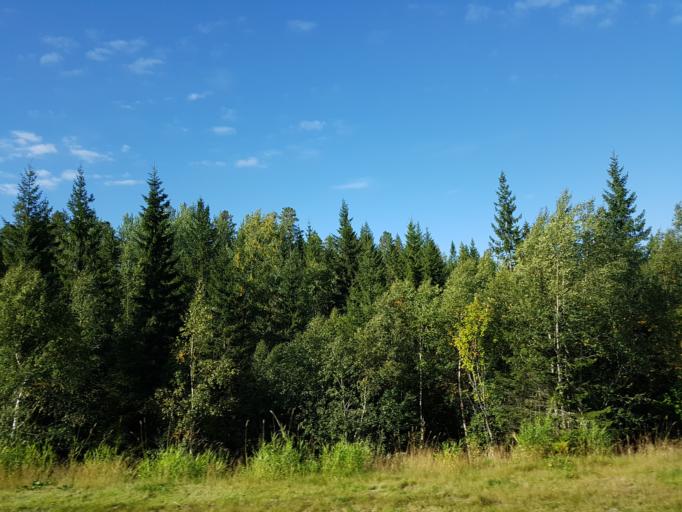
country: NO
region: Sor-Trondelag
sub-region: Trondheim
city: Trondheim
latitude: 63.6416
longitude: 10.2698
